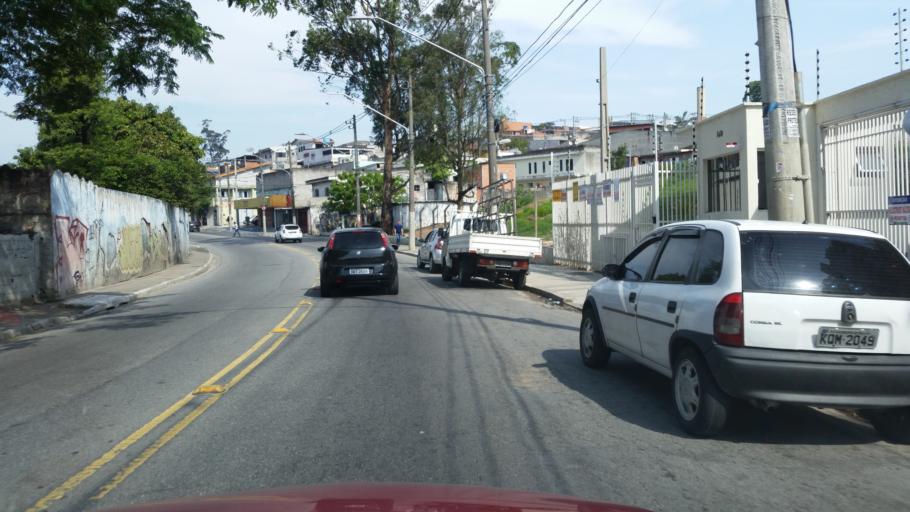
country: BR
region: Sao Paulo
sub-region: Ferraz De Vasconcelos
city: Ferraz de Vasconcelos
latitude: -23.5633
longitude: -46.4189
